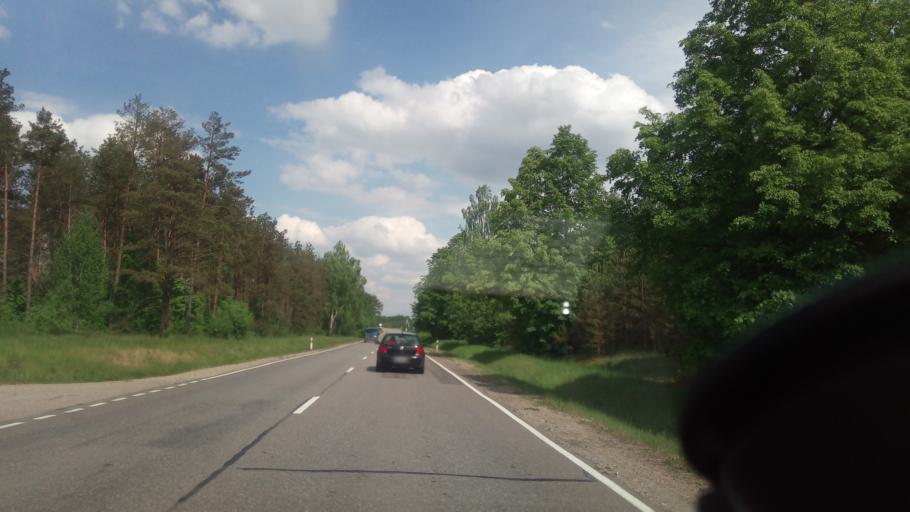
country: LT
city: Trakai
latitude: 54.6087
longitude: 24.8636
